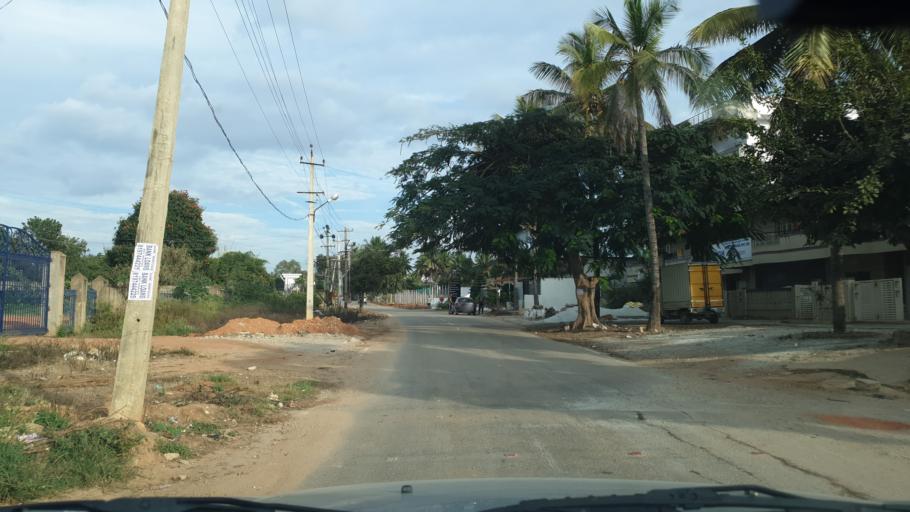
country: IN
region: Karnataka
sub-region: Bangalore Urban
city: Yelahanka
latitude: 13.1891
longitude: 77.6331
